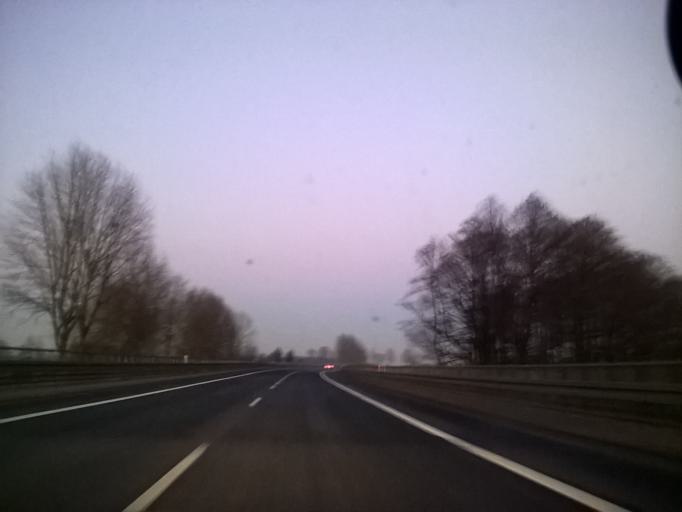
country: PL
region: Warmian-Masurian Voivodeship
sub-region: Powiat olsztynski
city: Czerwonka
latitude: 53.8279
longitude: 20.8715
